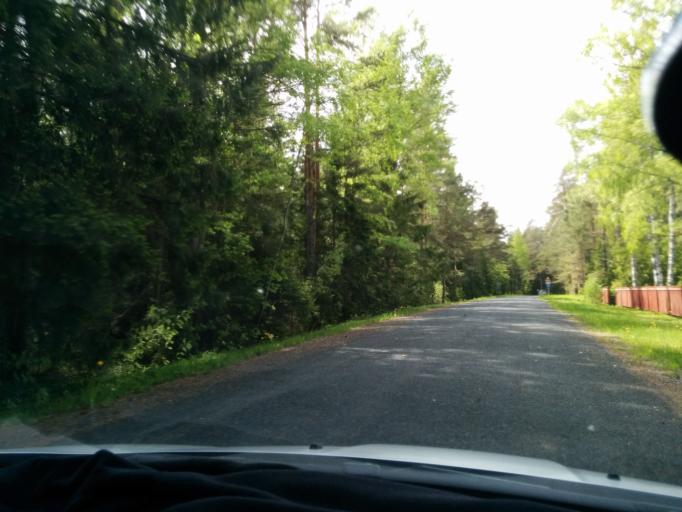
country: EE
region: Harju
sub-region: Loksa linn
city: Loksa
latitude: 59.5776
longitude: 25.6100
